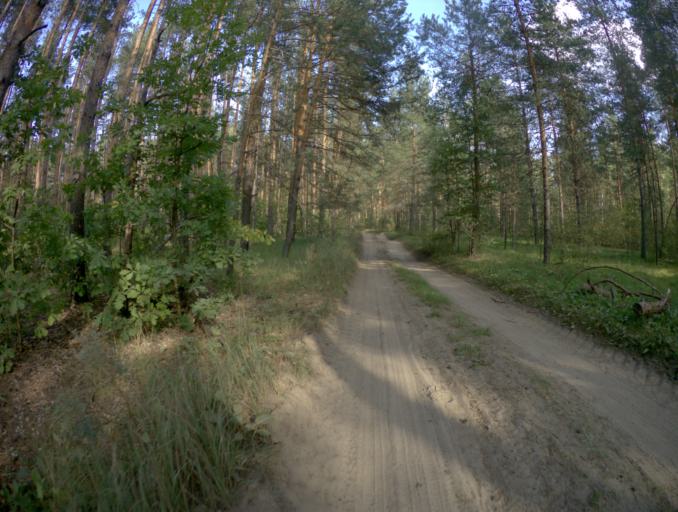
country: RU
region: Vladimir
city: Petushki
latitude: 55.8851
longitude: 39.4690
